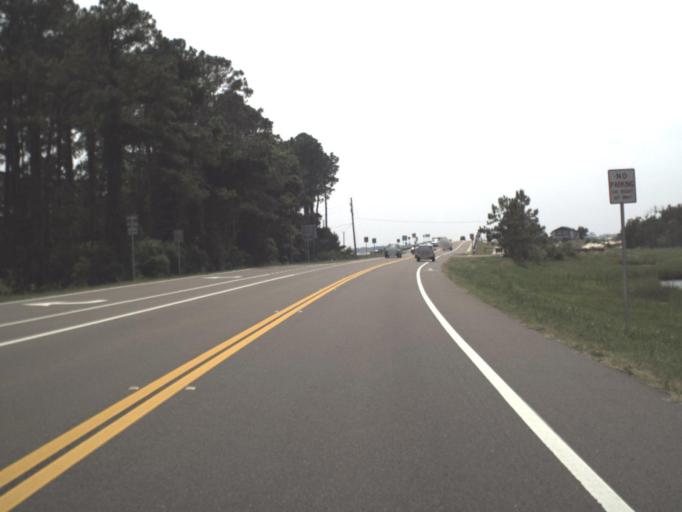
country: US
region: Florida
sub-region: Nassau County
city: Fernandina Beach
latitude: 30.5244
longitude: -81.4424
